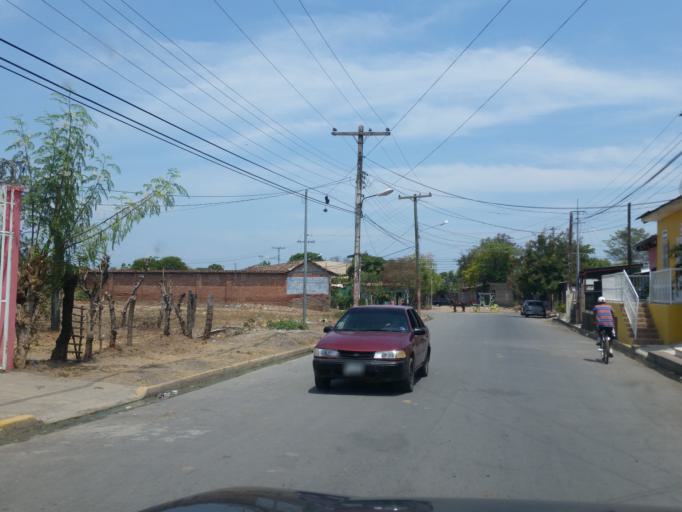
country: NI
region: Granada
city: Granada
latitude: 11.9343
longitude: -85.9490
